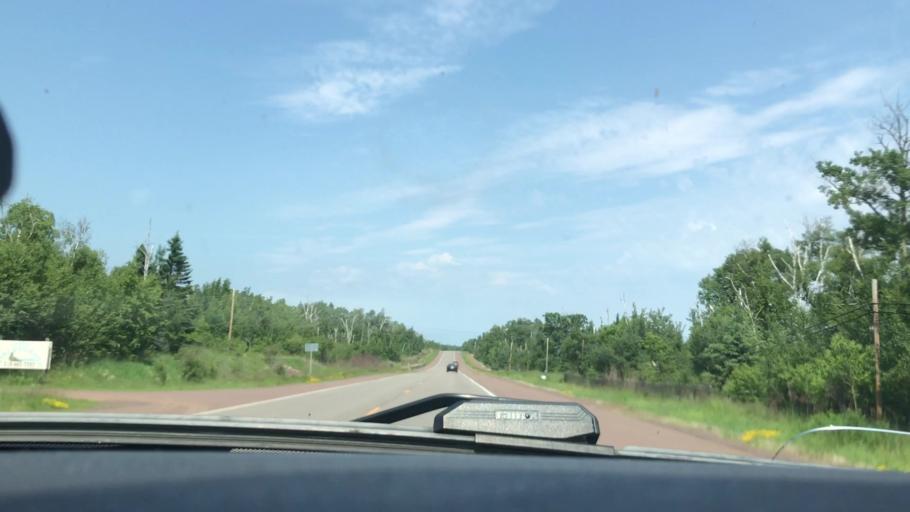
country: US
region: Minnesota
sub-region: Lake County
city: Silver Bay
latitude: 47.5799
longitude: -90.8244
